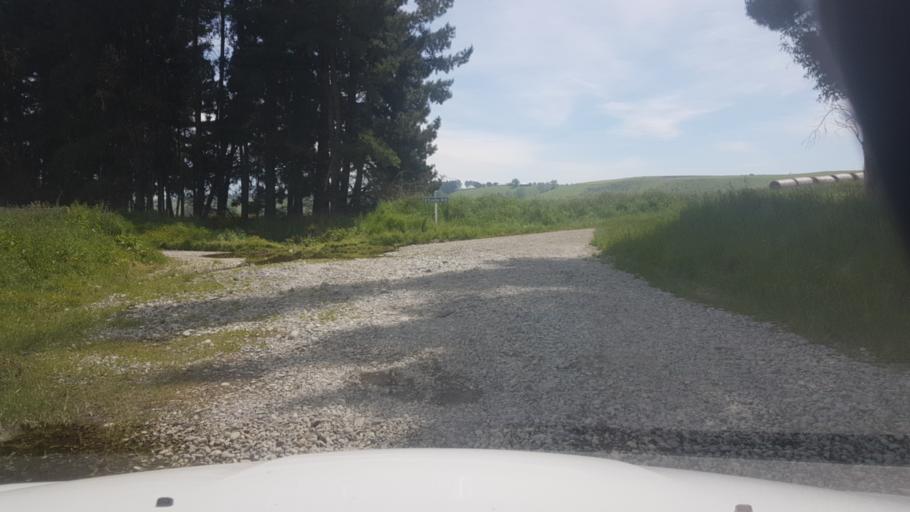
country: NZ
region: Canterbury
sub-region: Timaru District
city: Pleasant Point
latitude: -44.2204
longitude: 171.1625
